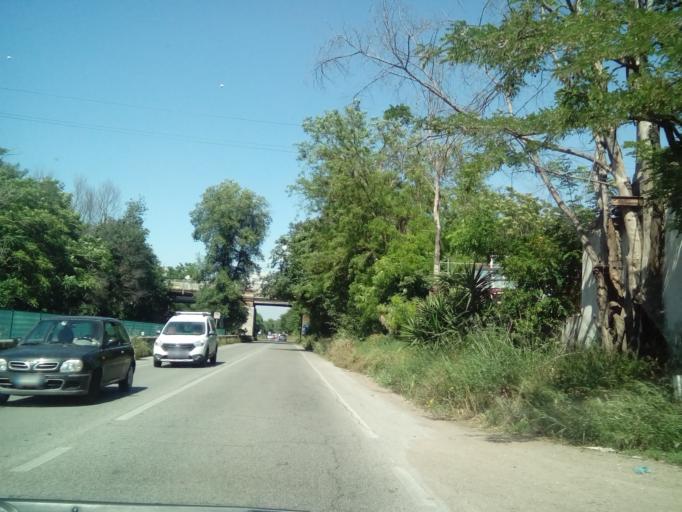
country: IT
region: Latium
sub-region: Citta metropolitana di Roma Capitale
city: Vitinia
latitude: 41.8351
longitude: 12.4567
